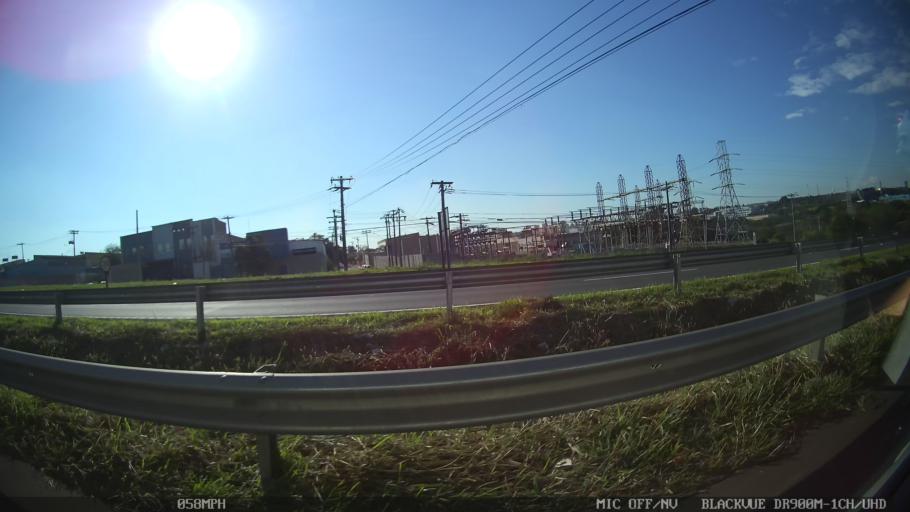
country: BR
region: Sao Paulo
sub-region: Americana
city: Americana
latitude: -22.7591
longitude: -47.3184
